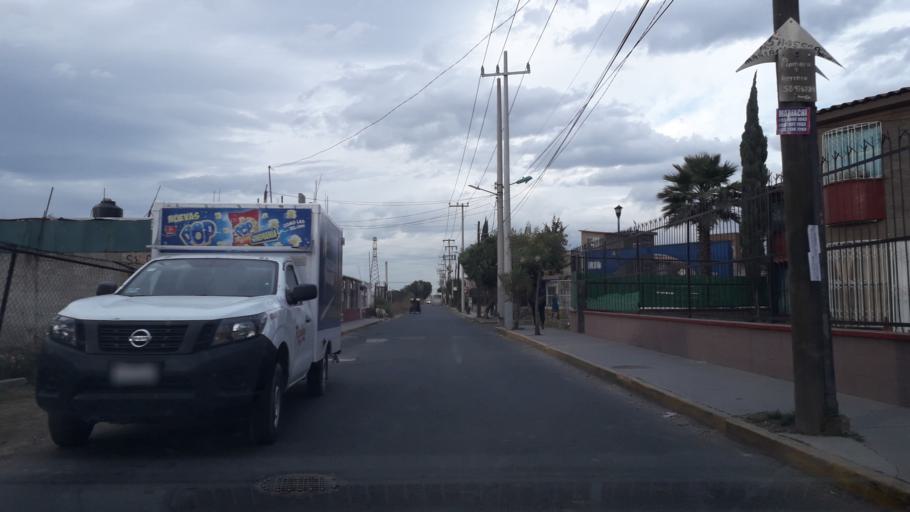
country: MX
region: Mexico
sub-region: Jaltenco
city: Alborada Jaltenco
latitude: 19.6673
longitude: -99.0697
